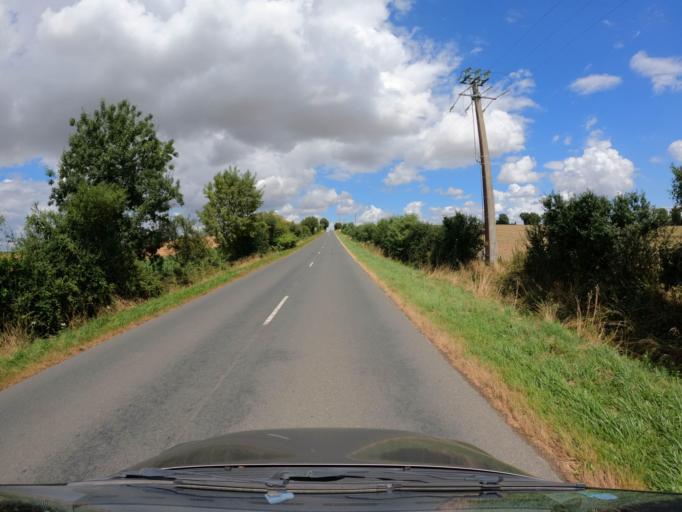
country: FR
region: Pays de la Loire
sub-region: Departement de Maine-et-Loire
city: Mire
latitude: 47.7459
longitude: -0.5034
